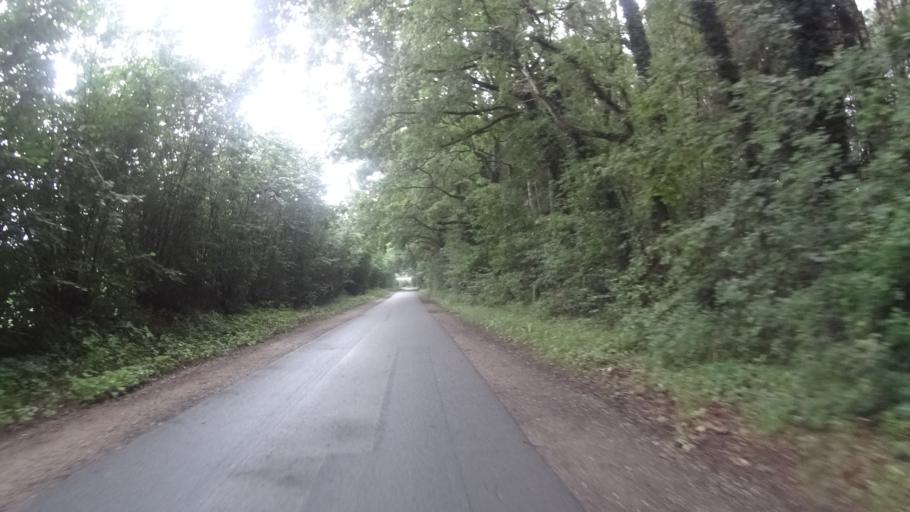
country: DE
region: Schleswig-Holstein
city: Roseburg
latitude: 53.5234
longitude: 10.6293
